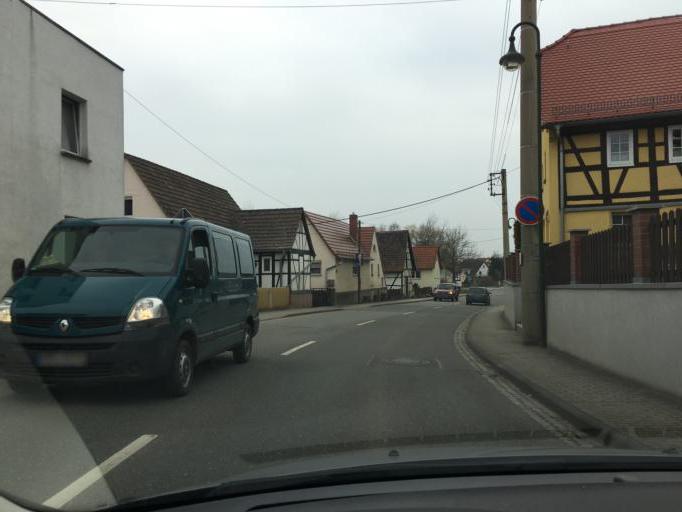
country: DE
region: Thuringia
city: Gerstenberg
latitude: 51.0285
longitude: 12.4418
